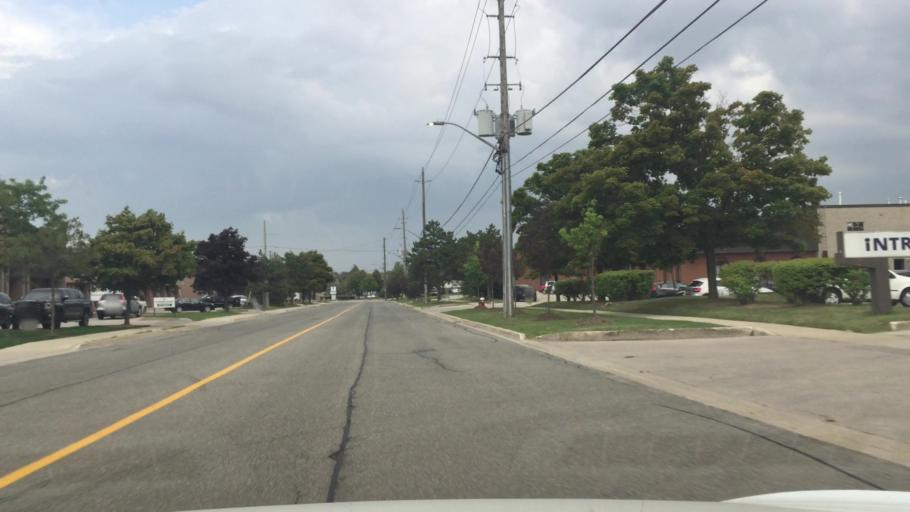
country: CA
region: Ontario
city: Mississauga
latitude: 43.6269
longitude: -79.6395
